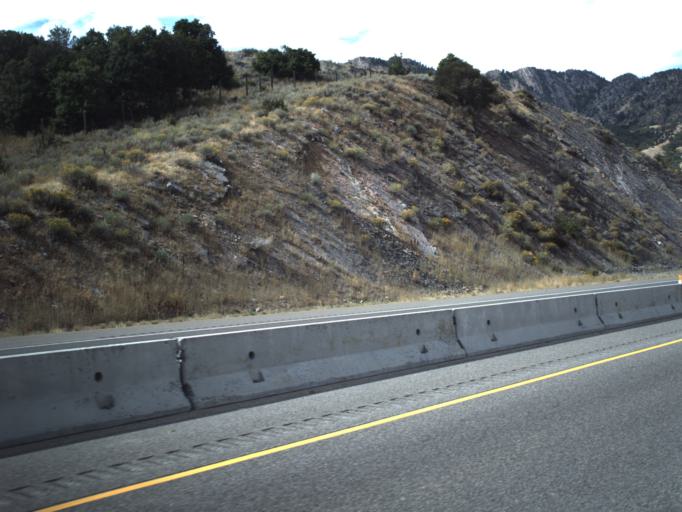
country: US
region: Utah
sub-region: Box Elder County
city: Brigham City
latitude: 41.5569
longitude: -111.9582
